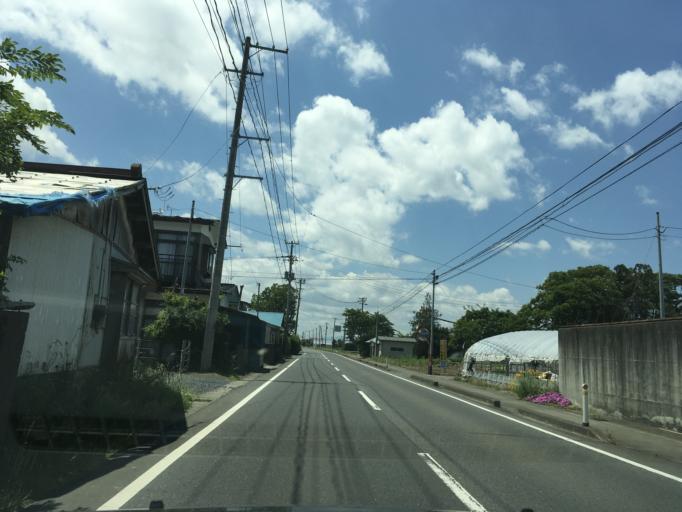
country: JP
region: Miyagi
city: Wakuya
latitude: 38.6768
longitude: 141.2472
